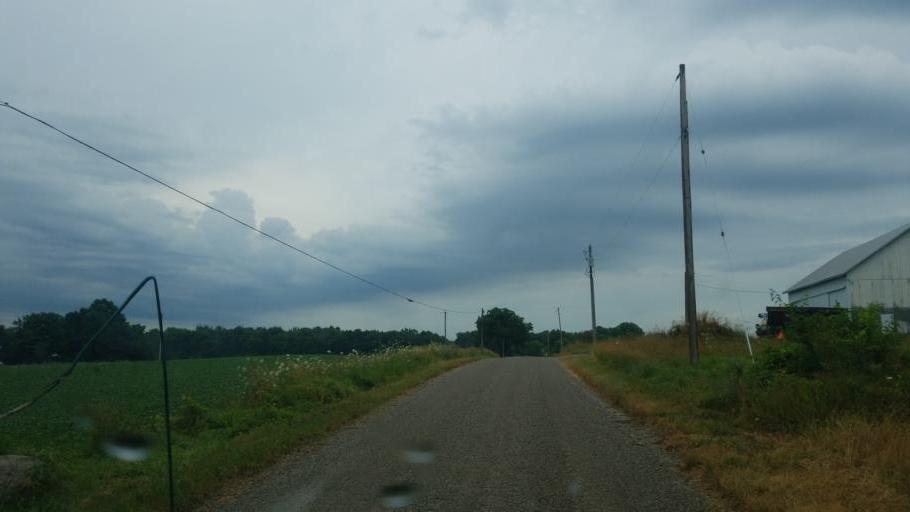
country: US
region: Indiana
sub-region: Steuben County
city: Hamilton
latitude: 41.5125
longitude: -84.9356
